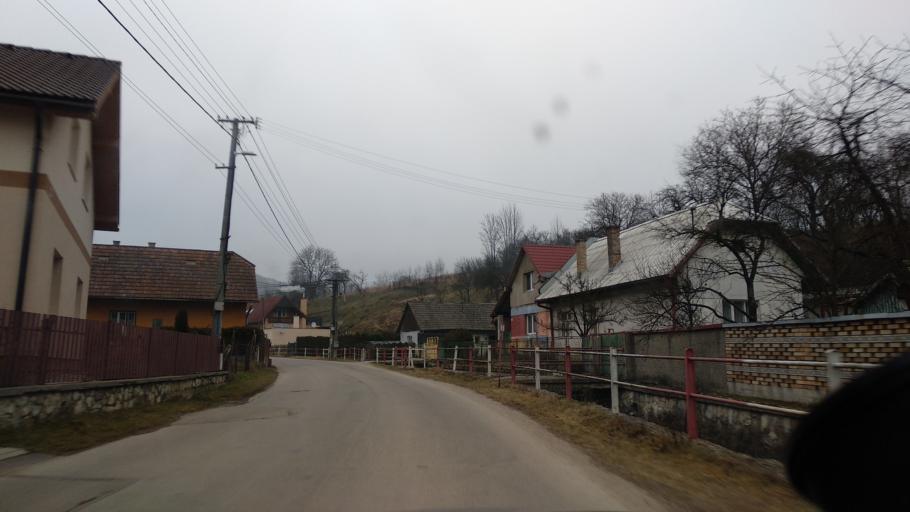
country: SK
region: Nitriansky
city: Ilava
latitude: 48.9094
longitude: 18.2949
